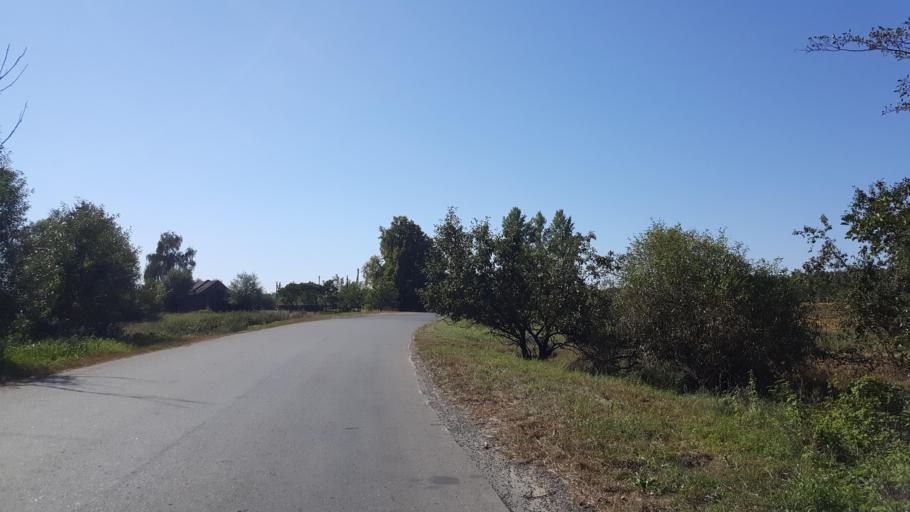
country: BY
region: Brest
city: Charnawchytsy
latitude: 52.3203
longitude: 23.6150
